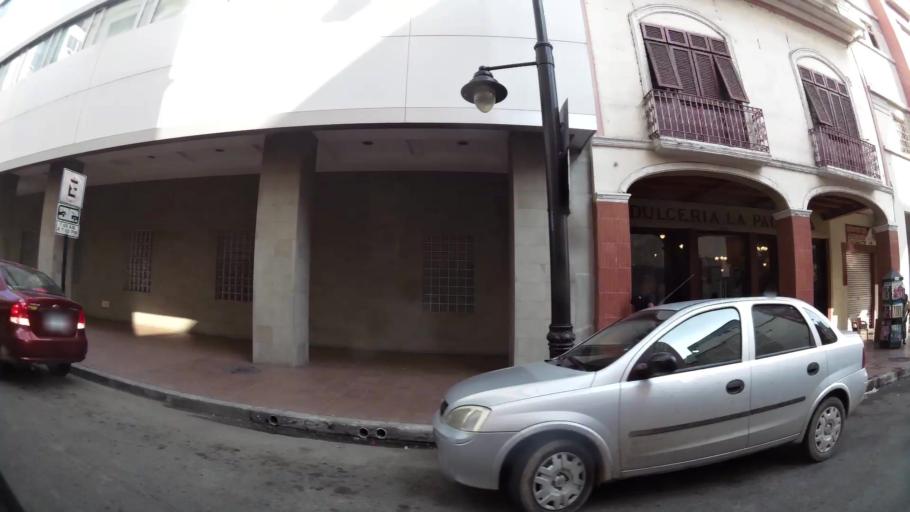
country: EC
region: Guayas
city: Guayaquil
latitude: -2.1922
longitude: -79.8836
